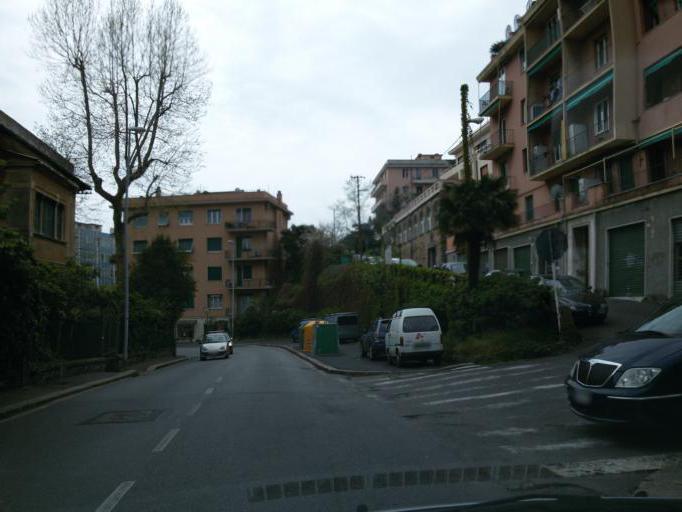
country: IT
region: Liguria
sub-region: Provincia di Genova
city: Genoa
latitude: 44.3977
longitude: 8.9803
